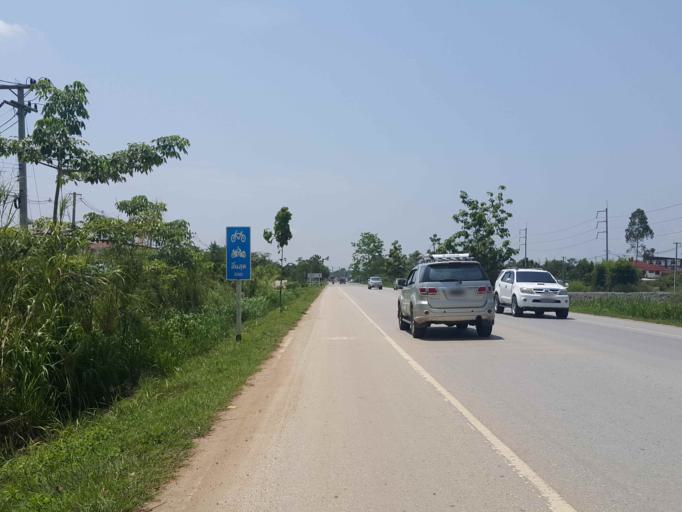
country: TH
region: Chiang Mai
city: San Sai
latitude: 18.8215
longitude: 99.0505
